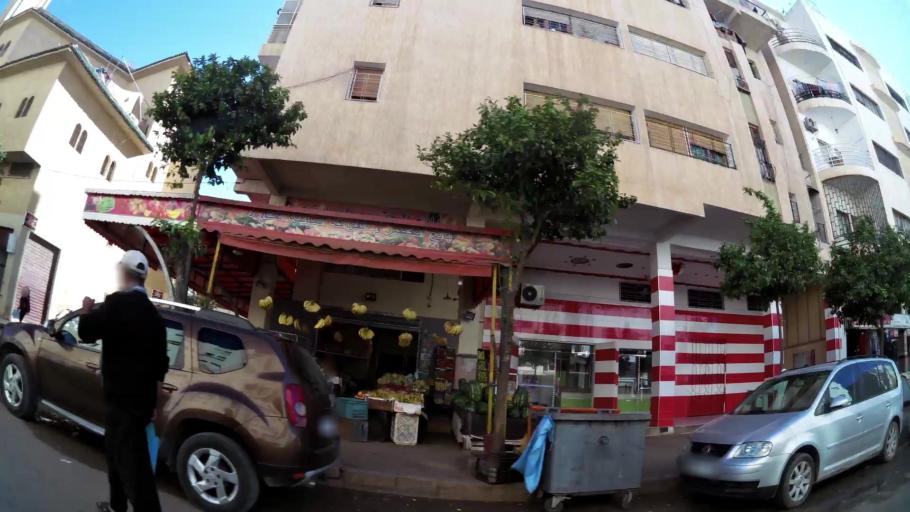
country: MA
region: Fes-Boulemane
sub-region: Fes
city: Fes
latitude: 34.0113
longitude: -4.9667
